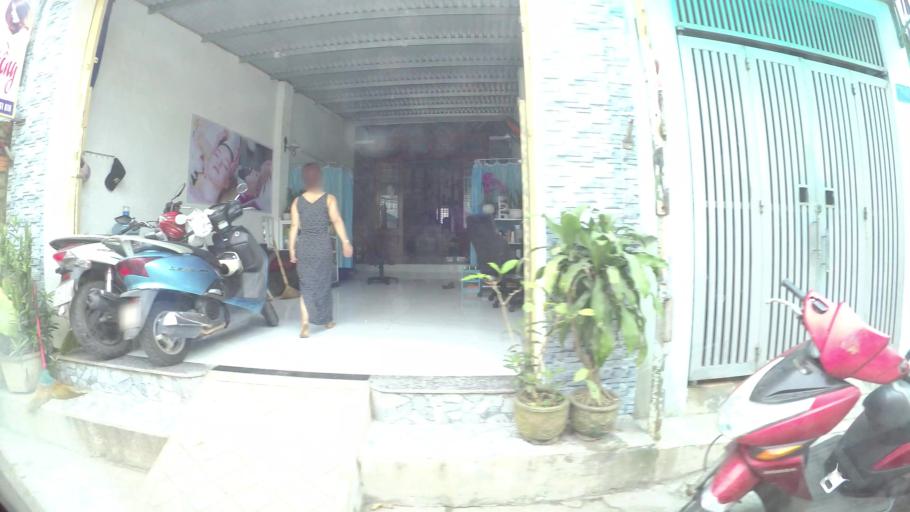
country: VN
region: Da Nang
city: Thanh Khe
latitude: 16.0675
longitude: 108.1967
